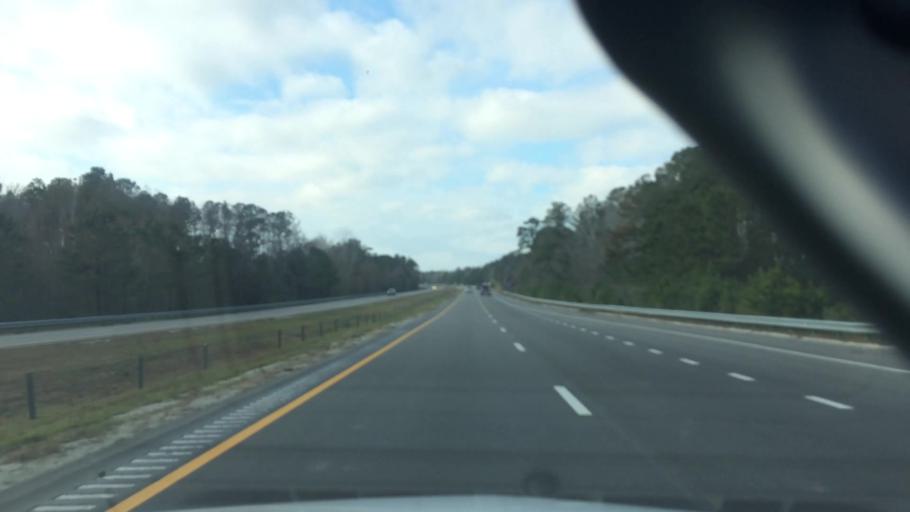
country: US
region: North Carolina
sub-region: New Hanover County
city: Wrightsboro
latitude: 34.3179
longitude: -77.9253
